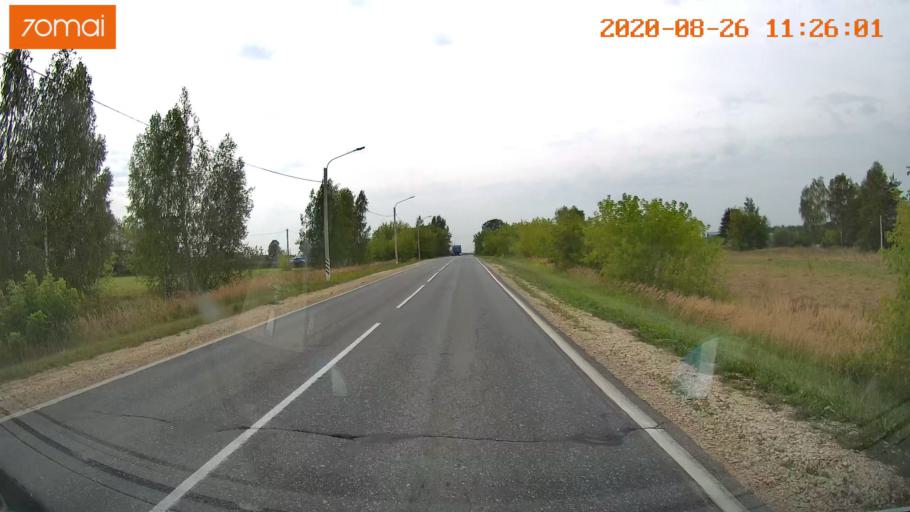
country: RU
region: Rjazan
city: Shilovo
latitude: 54.3369
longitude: 40.9550
